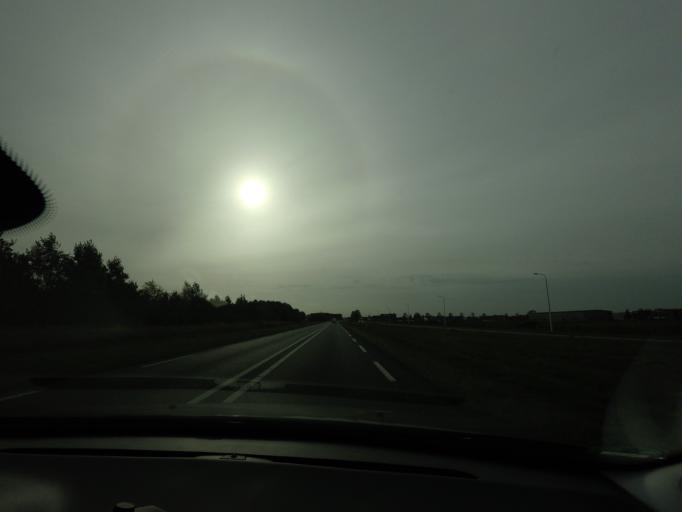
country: NL
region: Flevoland
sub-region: Gemeente Noordoostpolder
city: Emmeloord
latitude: 52.7129
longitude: 5.7924
